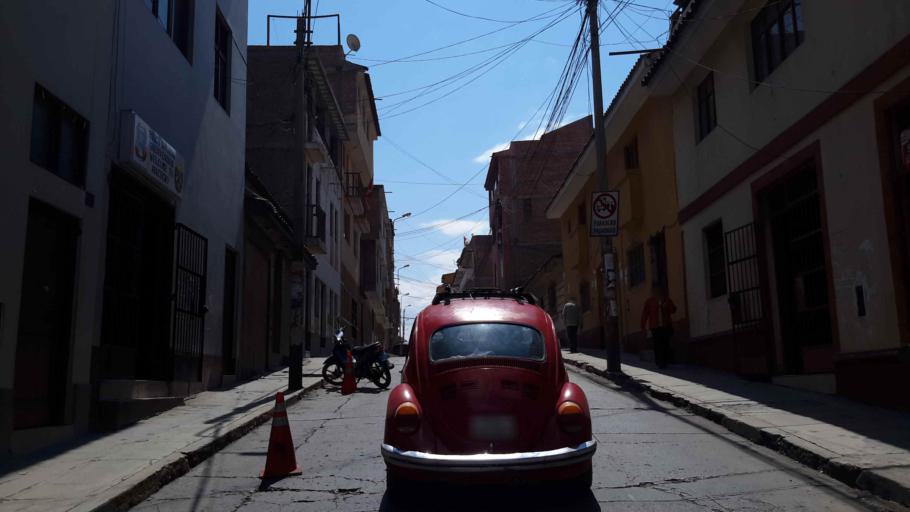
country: PE
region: Ayacucho
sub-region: Provincia de Huamanga
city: Ayacucho
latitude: -13.1615
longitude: -74.2230
